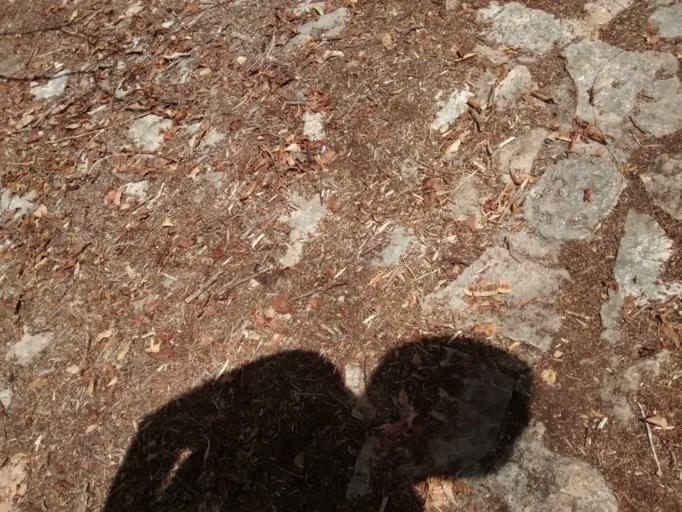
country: MX
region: Yucatan
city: Temozon
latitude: 20.8924
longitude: -88.1372
